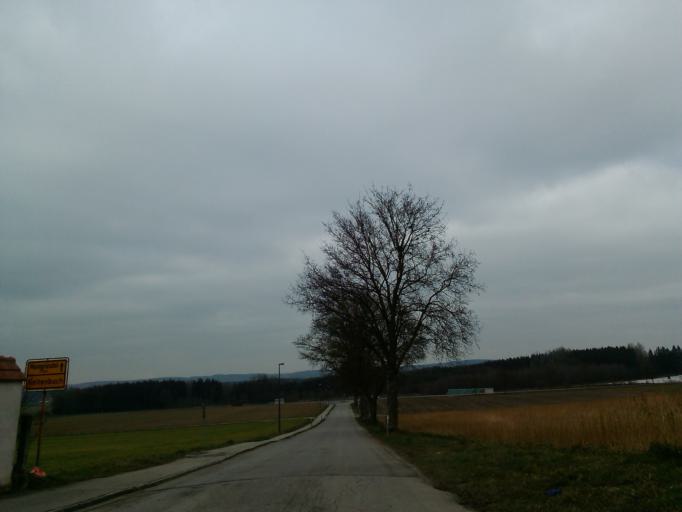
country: DE
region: Bavaria
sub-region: Swabia
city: Ustersbach
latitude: 48.3188
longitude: 10.6743
